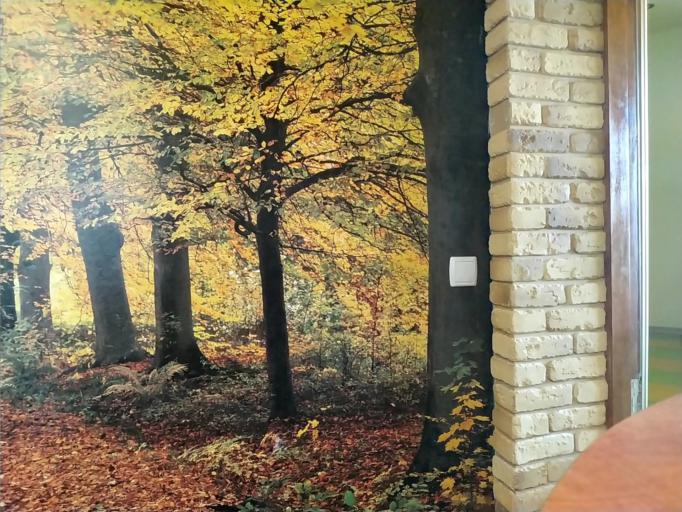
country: RU
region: Arkhangelskaya
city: Kargopol'
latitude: 60.7994
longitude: 38.8894
